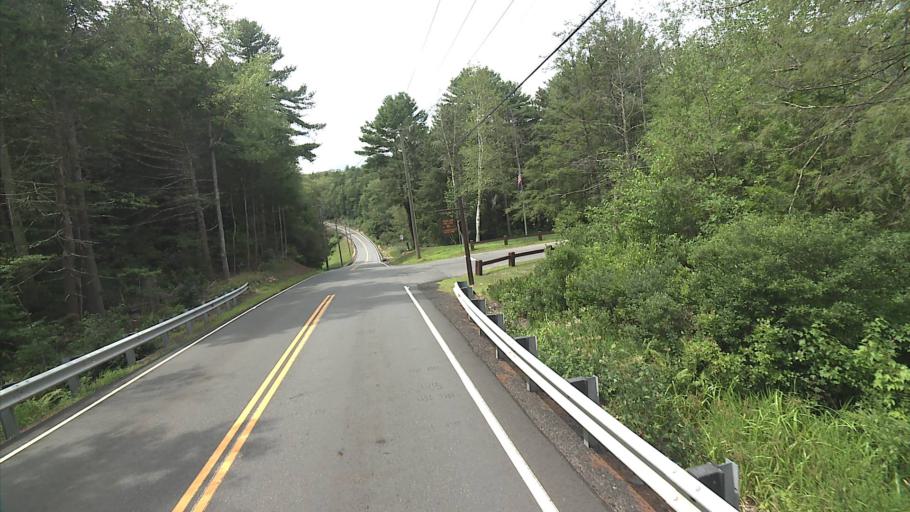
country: US
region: Massachusetts
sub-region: Hampden County
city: Holland
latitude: 41.9913
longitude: -72.1301
